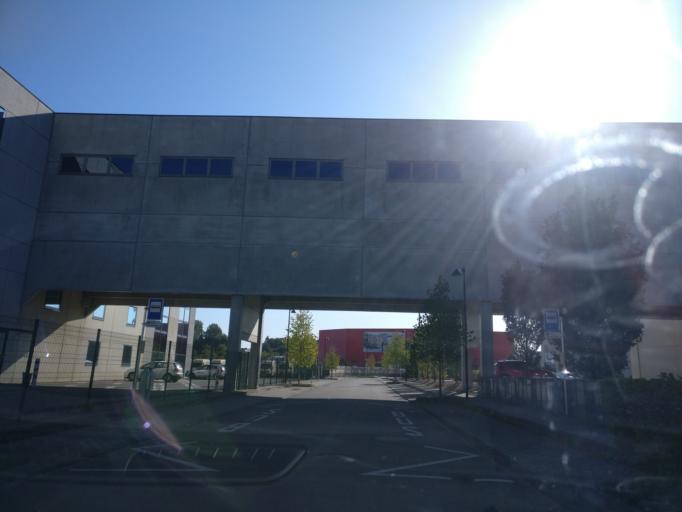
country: LU
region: Luxembourg
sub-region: Canton de Capellen
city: Mamer
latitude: 49.6418
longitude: 6.0122
